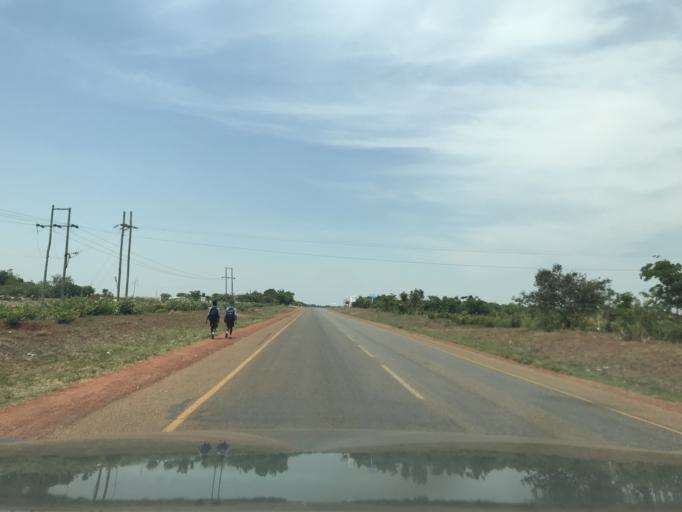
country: ZM
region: Northern
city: Kasama
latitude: -10.2174
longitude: 31.1447
